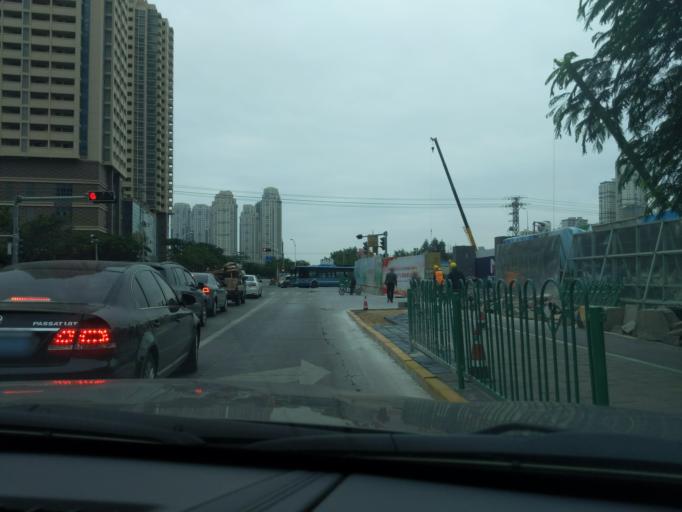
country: CN
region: Fujian
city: Xiamen
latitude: 24.4878
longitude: 118.1576
